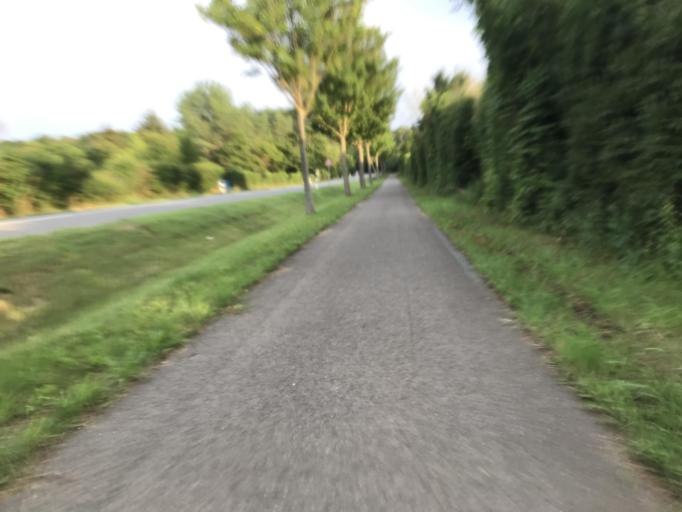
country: DE
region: Saxony-Anhalt
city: Quedlinburg
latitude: 51.8047
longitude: 11.1307
